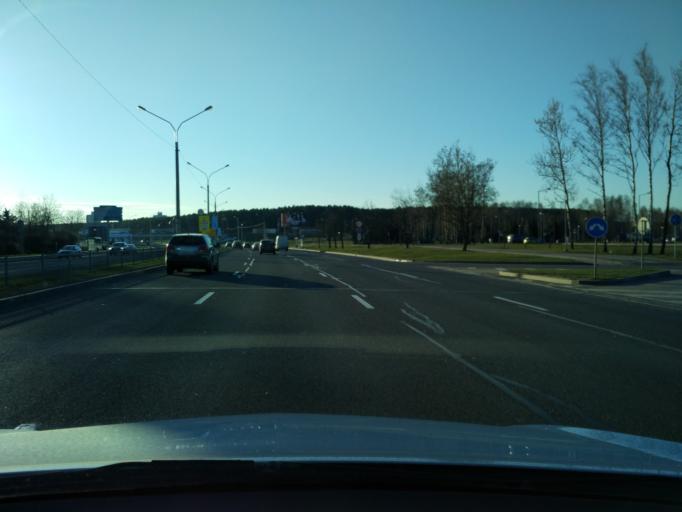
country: BY
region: Minsk
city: Zhdanovichy
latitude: 53.9488
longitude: 27.4517
